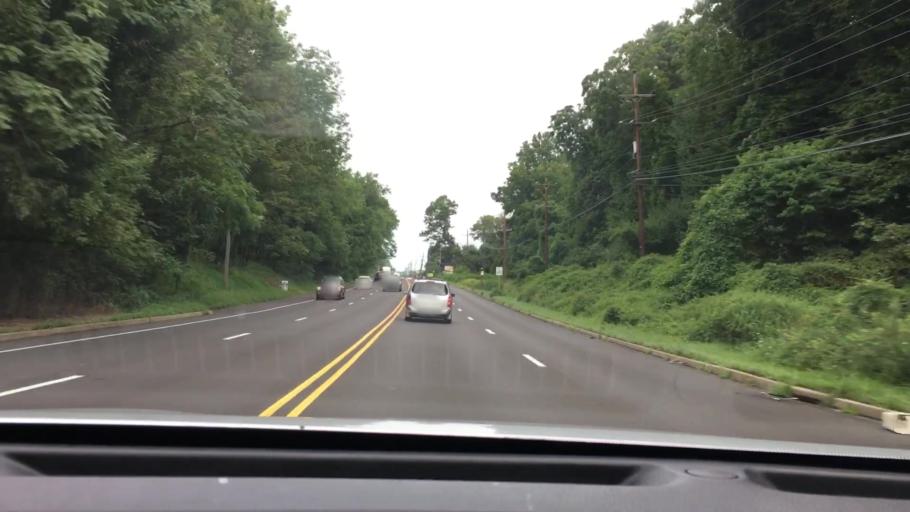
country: US
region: Pennsylvania
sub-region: Bucks County
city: Warminster Heights
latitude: 40.1743
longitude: -75.0765
